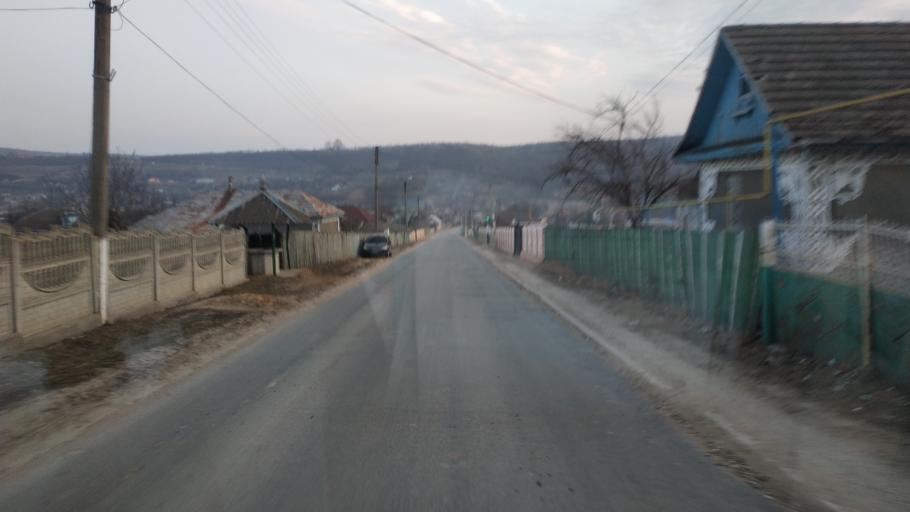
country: MD
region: Hincesti
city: Dancu
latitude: 46.6689
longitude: 28.3278
